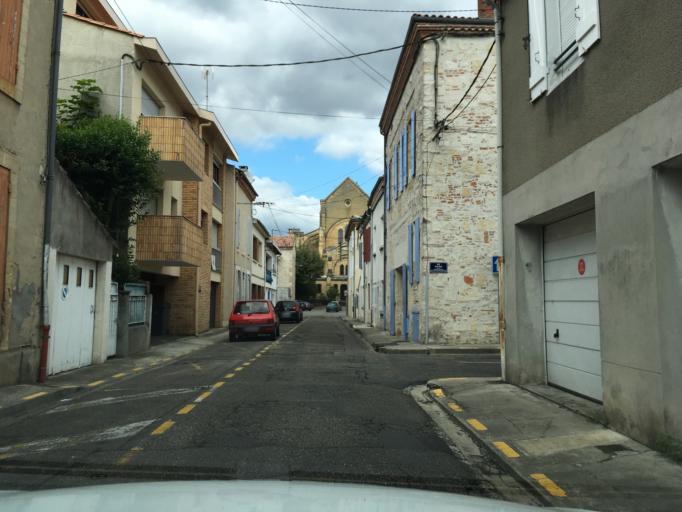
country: FR
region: Aquitaine
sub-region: Departement du Lot-et-Garonne
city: Agen
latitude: 44.2019
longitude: 0.6262
